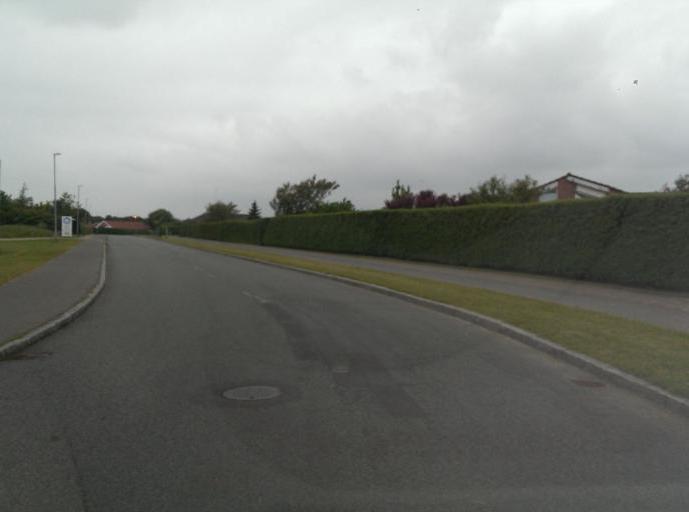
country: DK
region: South Denmark
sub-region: Fano Kommune
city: Nordby
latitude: 55.5308
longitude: 8.3676
